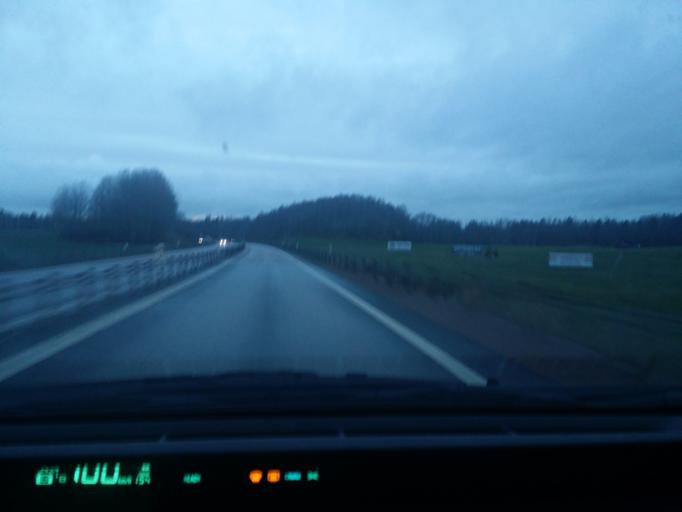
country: SE
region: Soedermanland
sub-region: Eskilstuna Kommun
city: Kvicksund
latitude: 59.4397
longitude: 16.3510
